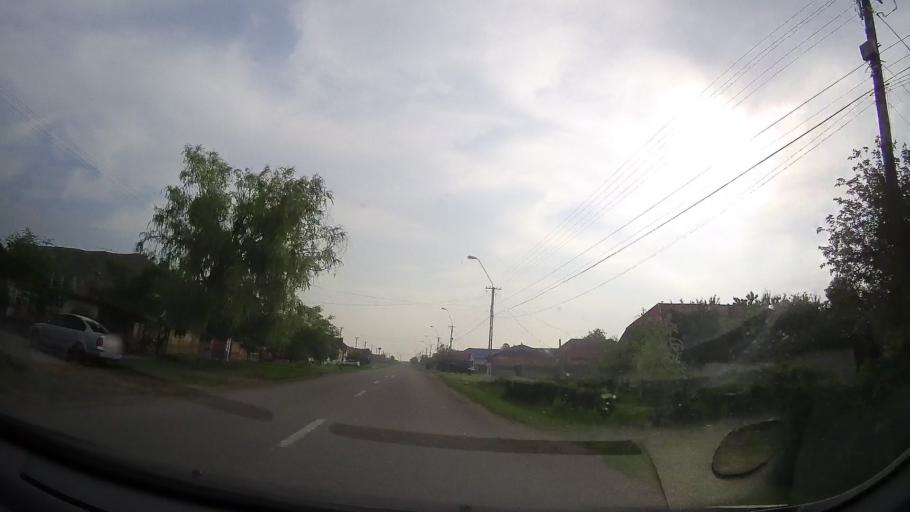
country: RO
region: Timis
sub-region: Comuna Foeni
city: Foeni
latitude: 45.5012
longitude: 20.8739
